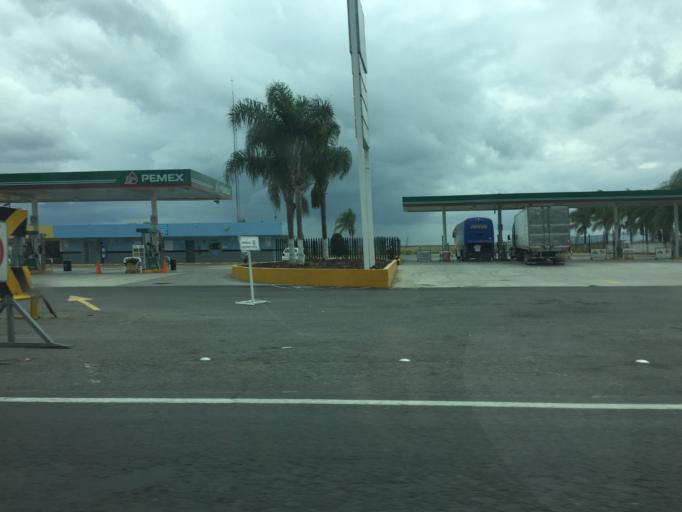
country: MX
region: Jalisco
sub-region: Tonala
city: Mismaloya (Fraccionamiento Pedregal de Santa Martha)
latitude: 20.6046
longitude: -103.1289
